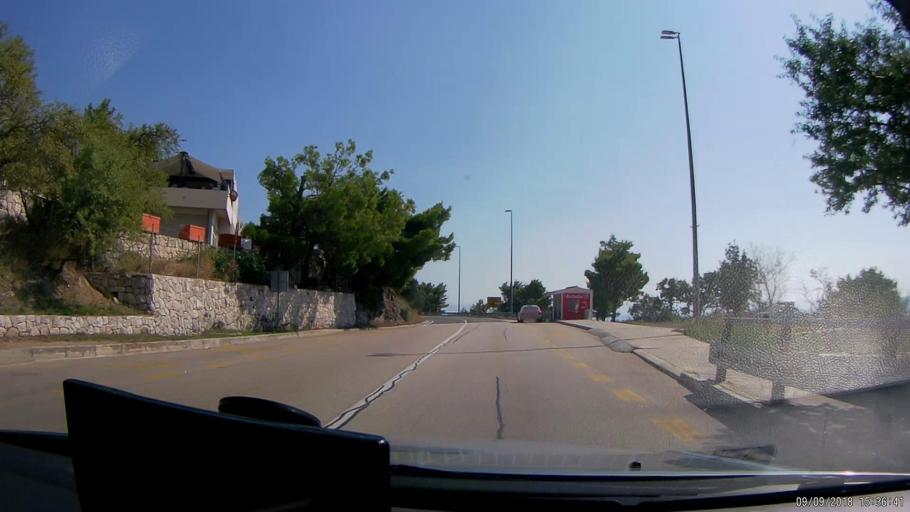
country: HR
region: Splitsko-Dalmatinska
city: Donja Brela
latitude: 43.3764
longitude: 16.9234
